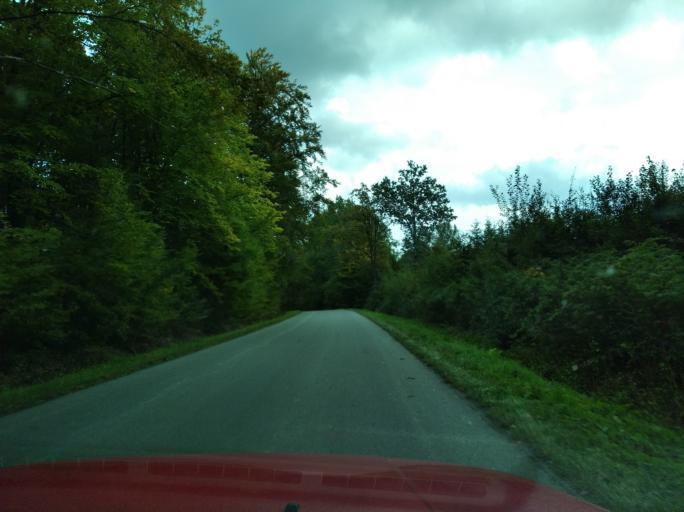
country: PL
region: Subcarpathian Voivodeship
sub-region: Powiat rzeszowski
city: Straszydle
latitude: 49.9312
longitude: 21.9990
